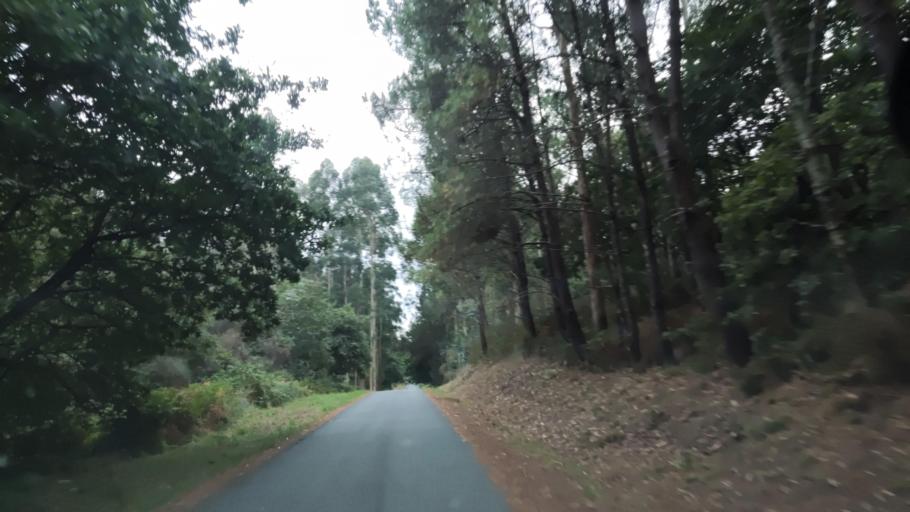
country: ES
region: Galicia
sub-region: Provincia da Coruna
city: Padron
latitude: 42.7187
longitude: -8.6819
